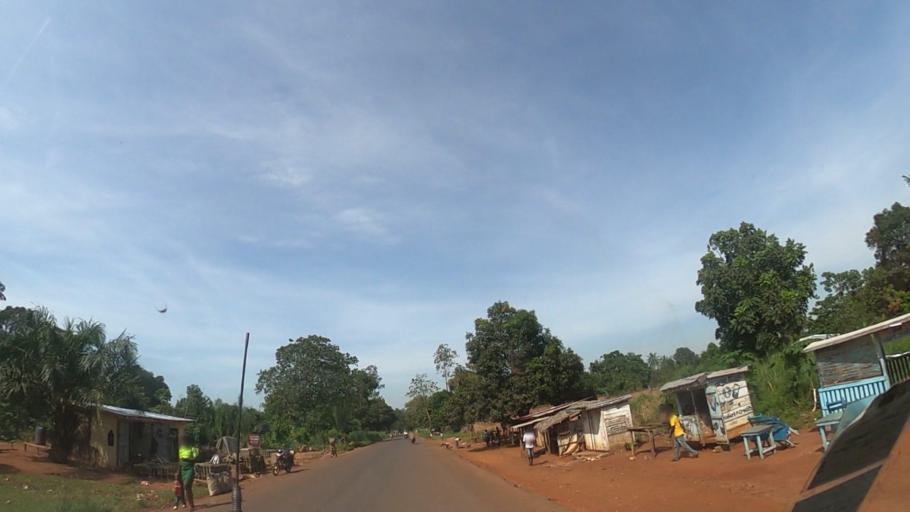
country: CF
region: Bangui
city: Bangui
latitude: 4.3124
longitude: 18.4862
